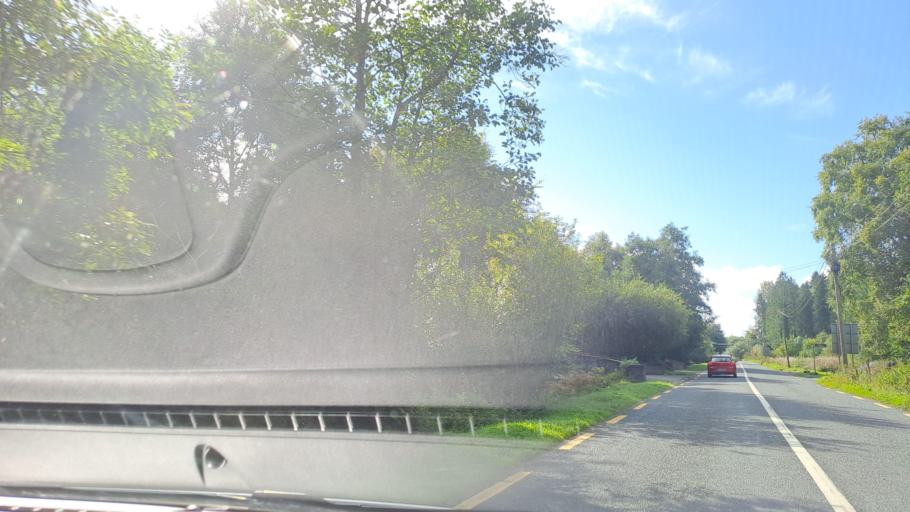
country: IE
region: Ulster
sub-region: An Cabhan
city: Kingscourt
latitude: 53.9125
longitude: -6.7875
